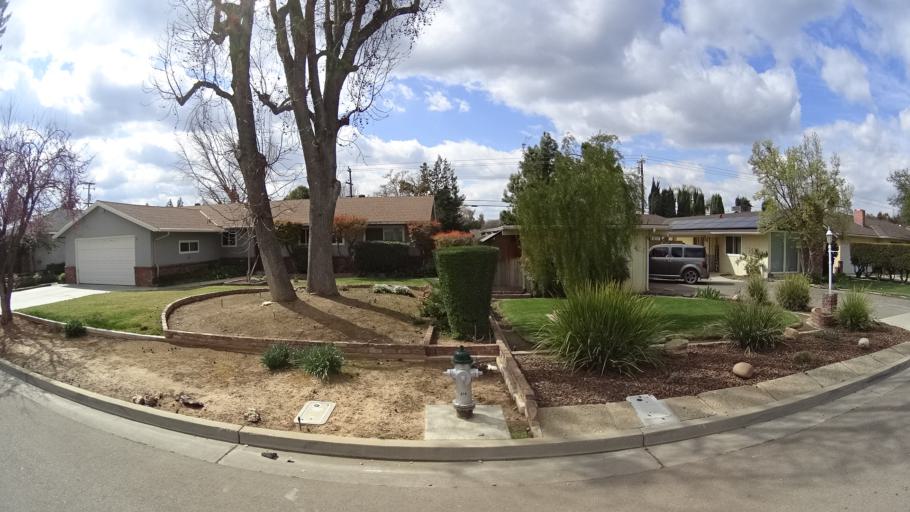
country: US
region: California
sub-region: Fresno County
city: Clovis
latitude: 36.8203
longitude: -119.7650
